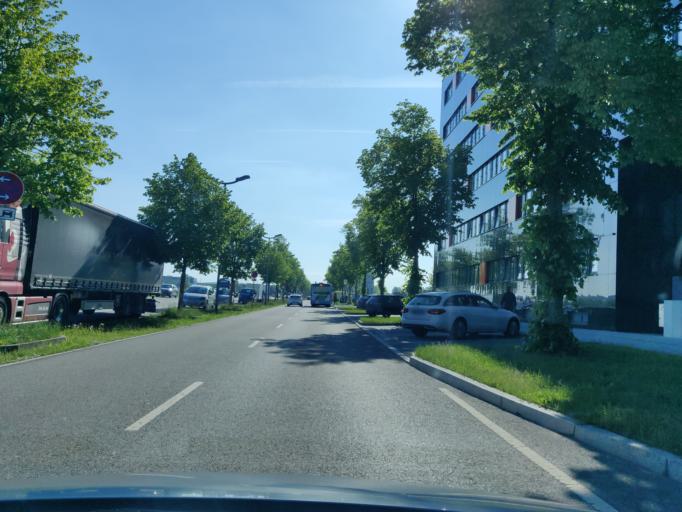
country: DE
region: Baden-Wuerttemberg
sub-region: Regierungsbezirk Stuttgart
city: Boeblingen
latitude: 48.6905
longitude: 8.9976
